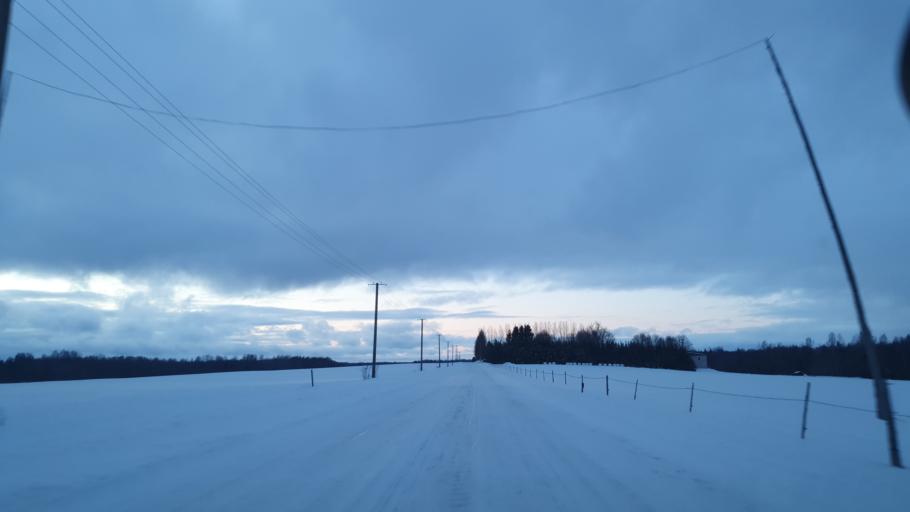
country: EE
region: Jogevamaa
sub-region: Tabivere vald
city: Tabivere
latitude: 58.5764
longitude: 26.5582
